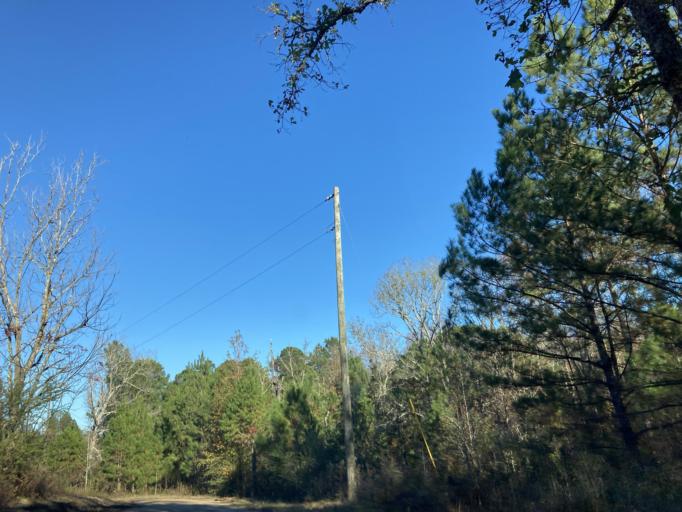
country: US
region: Mississippi
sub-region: Lamar County
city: Sumrall
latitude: 31.3890
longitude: -89.5640
